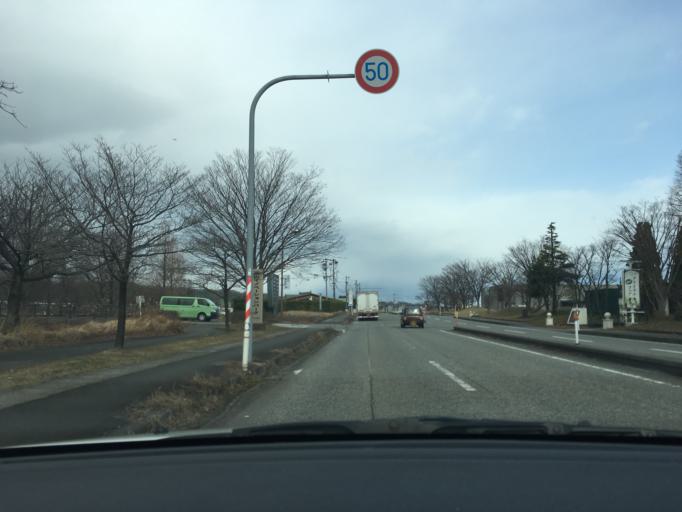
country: JP
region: Toyama
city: Toyama-shi
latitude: 36.6797
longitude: 137.1733
